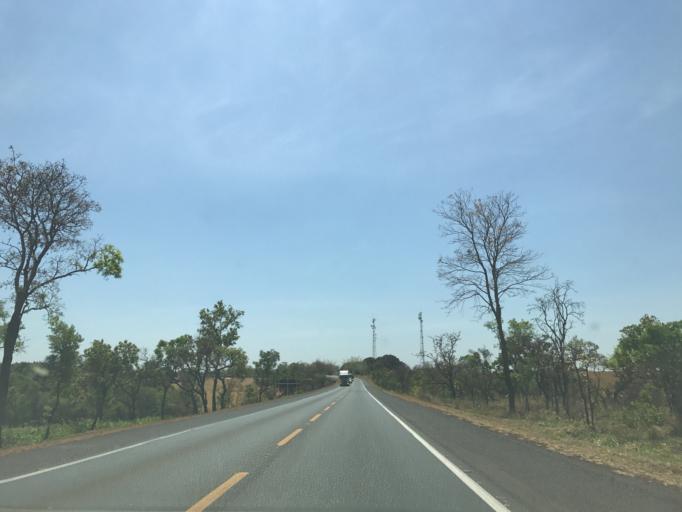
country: BR
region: Minas Gerais
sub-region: Frutal
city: Frutal
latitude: -19.8597
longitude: -48.9644
